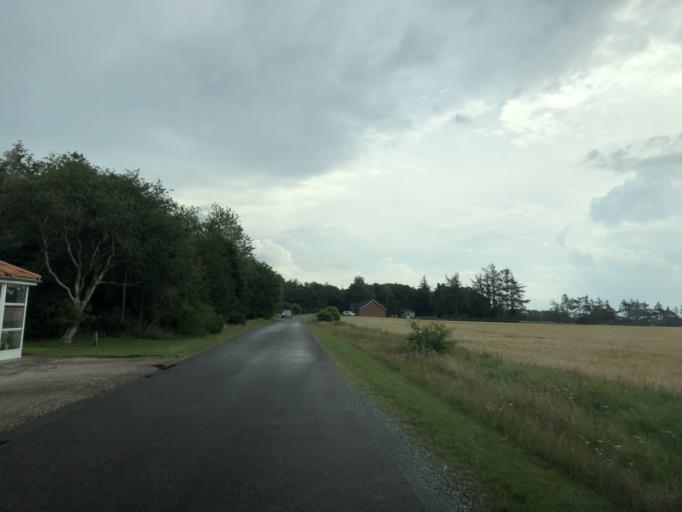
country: DK
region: Central Jutland
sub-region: Ringkobing-Skjern Kommune
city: Skjern
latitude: 55.8884
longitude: 8.4176
